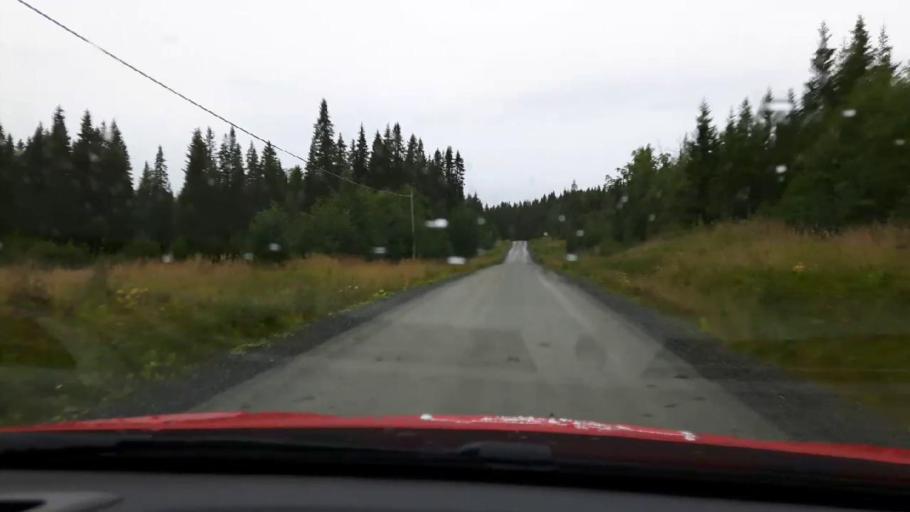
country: SE
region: Jaemtland
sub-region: Are Kommun
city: Are
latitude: 63.4837
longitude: 12.7915
